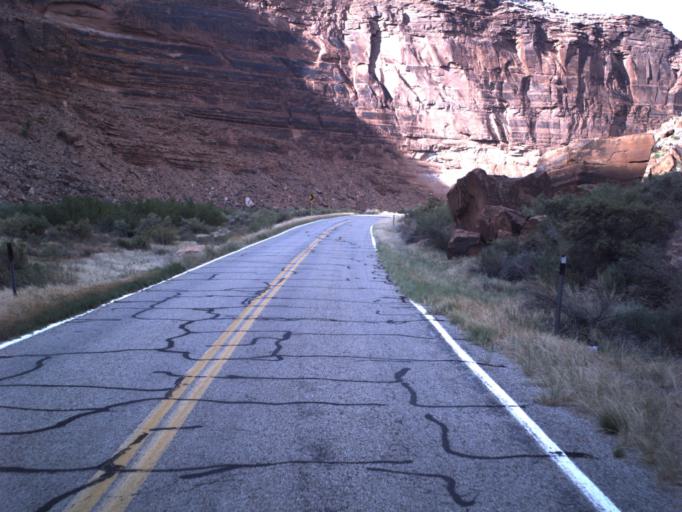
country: US
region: Utah
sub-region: Grand County
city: Moab
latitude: 38.8014
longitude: -109.3397
